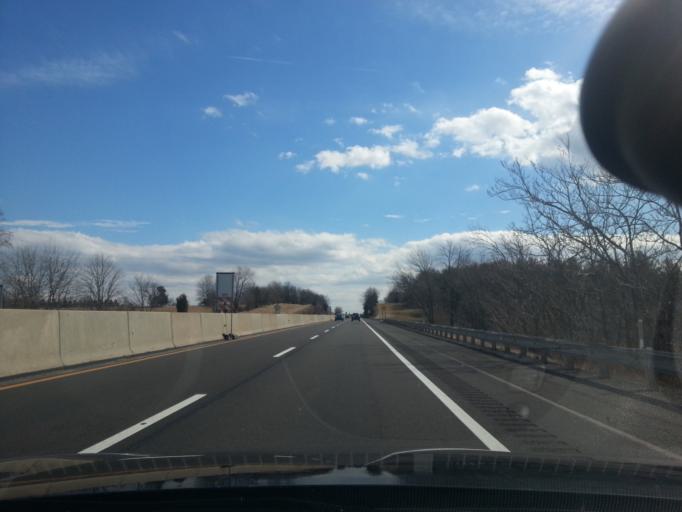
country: US
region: Pennsylvania
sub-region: Montgomery County
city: Harleysville
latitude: 40.3077
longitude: -75.3727
